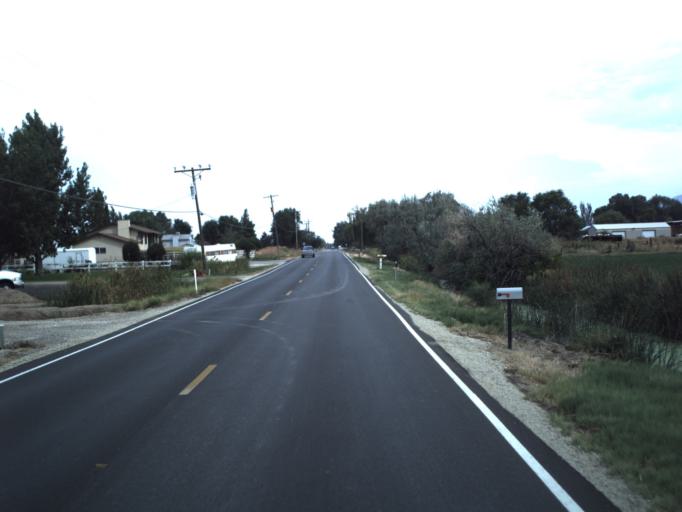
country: US
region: Utah
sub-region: Weber County
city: Plain City
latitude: 41.2578
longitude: -112.0924
